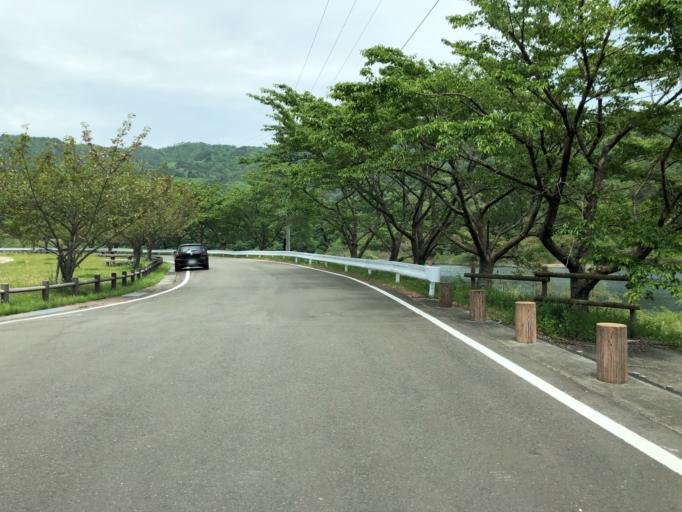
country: JP
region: Miyagi
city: Marumori
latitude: 37.7309
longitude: 140.8087
